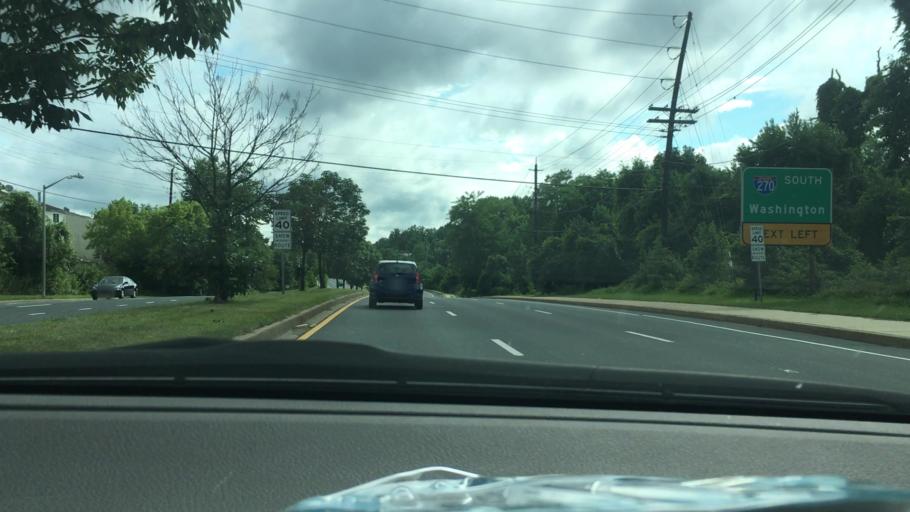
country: US
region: Maryland
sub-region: Montgomery County
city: Germantown
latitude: 39.1780
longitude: -77.2426
